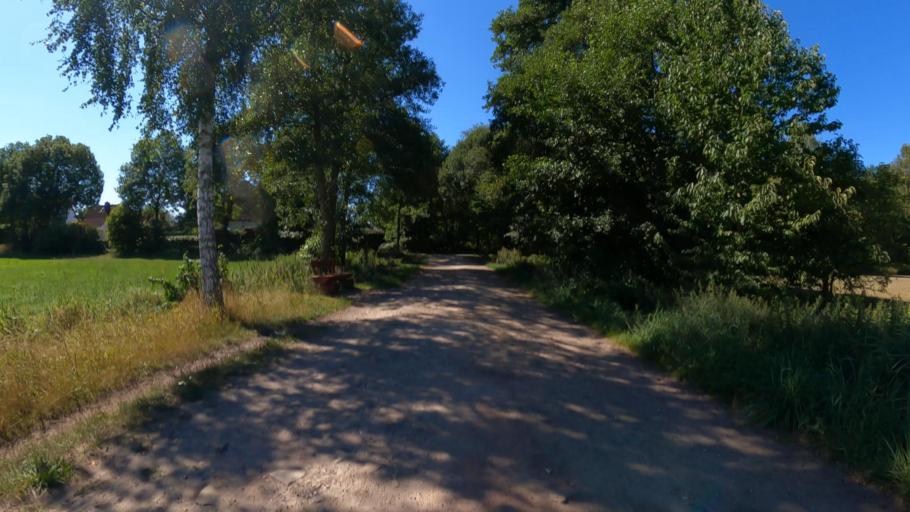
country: DE
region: Schleswig-Holstein
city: Escheburg
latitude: 53.4462
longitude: 10.3406
